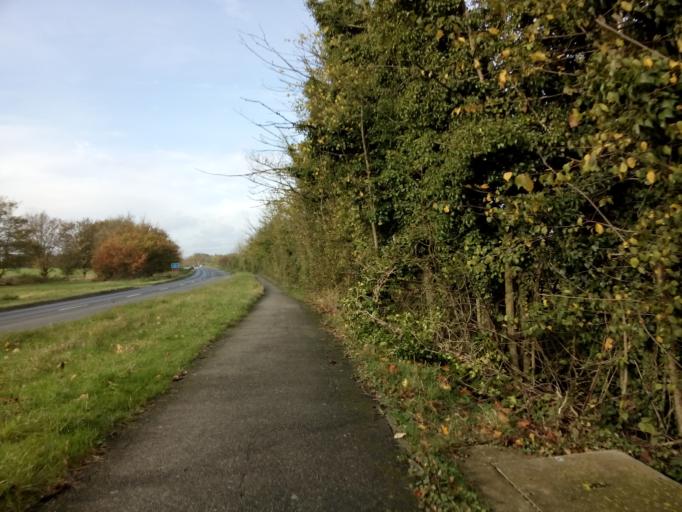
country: GB
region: England
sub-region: Suffolk
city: Needham Market
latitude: 52.1700
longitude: 1.0264
